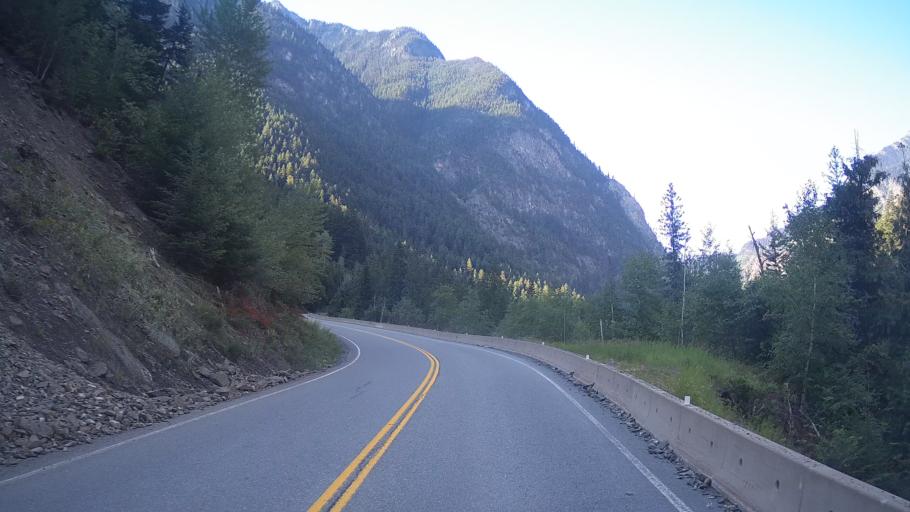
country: CA
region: British Columbia
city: Lillooet
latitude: 50.6368
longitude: -122.0889
